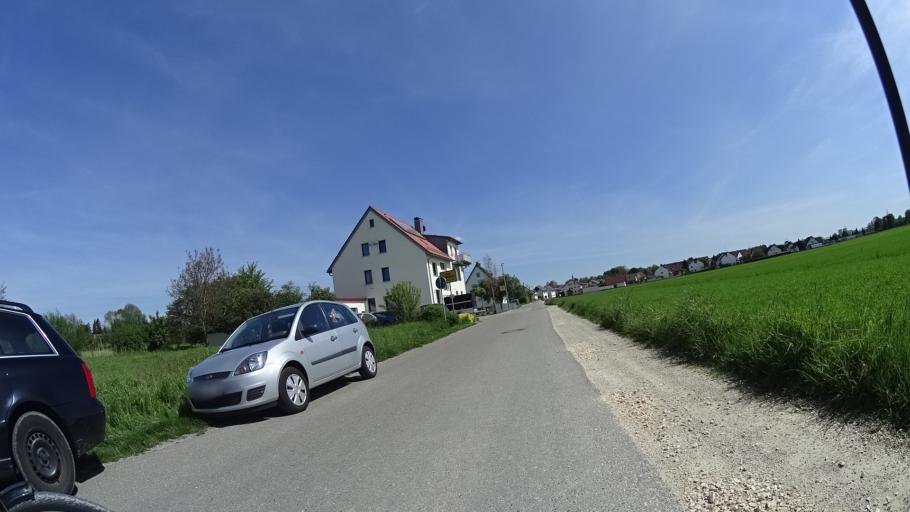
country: DE
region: Bavaria
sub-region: Swabia
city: Weissenhorn
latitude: 48.3131
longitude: 10.1517
